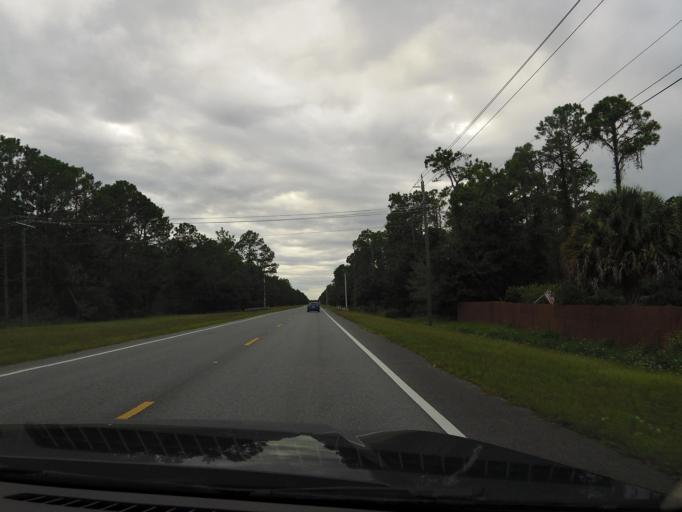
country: US
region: Florida
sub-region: Flagler County
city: Bunnell
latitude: 29.4973
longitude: -81.2387
